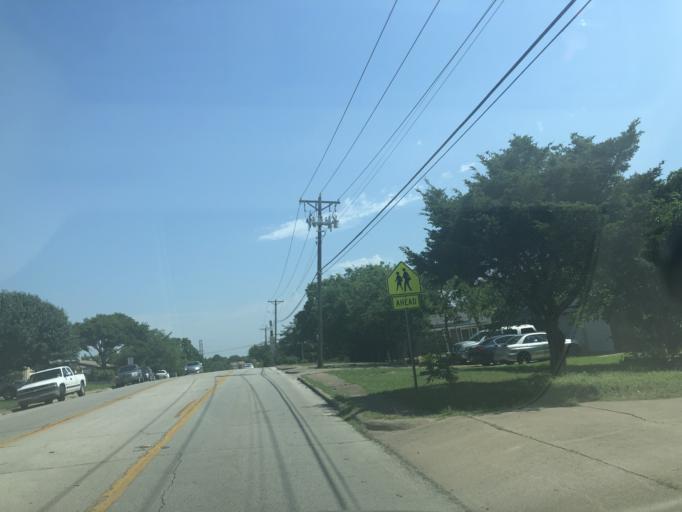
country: US
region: Texas
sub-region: Dallas County
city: Grand Prairie
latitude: 32.7227
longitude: -97.0071
